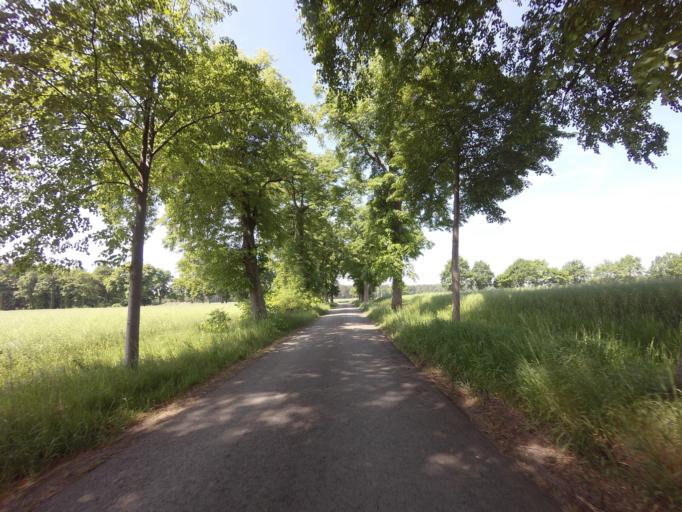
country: DE
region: Lower Saxony
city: Adenbuettel
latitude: 52.3787
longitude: 10.4394
